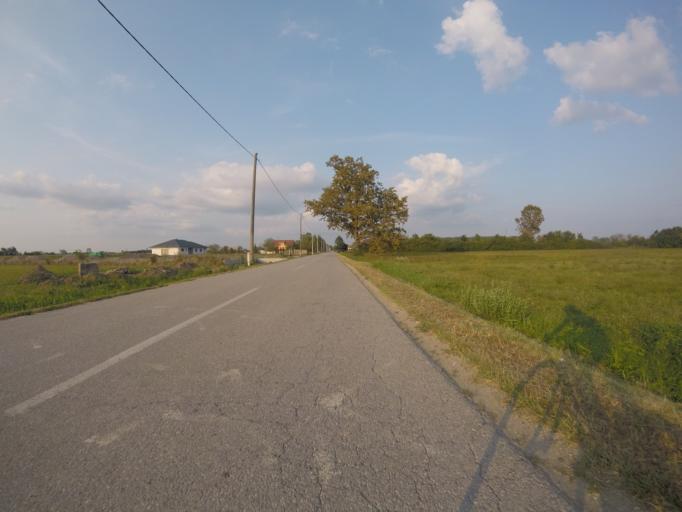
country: HR
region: Zagrebacka
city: Kuce
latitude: 45.7183
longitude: 16.1997
